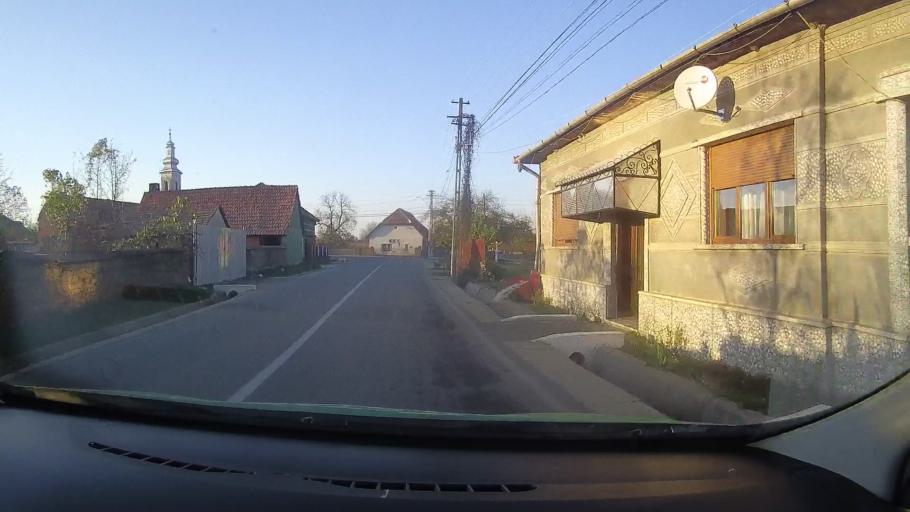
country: RO
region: Timis
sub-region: Comuna Traian Vuia
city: Traian Vuia
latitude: 45.7662
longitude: 22.0950
